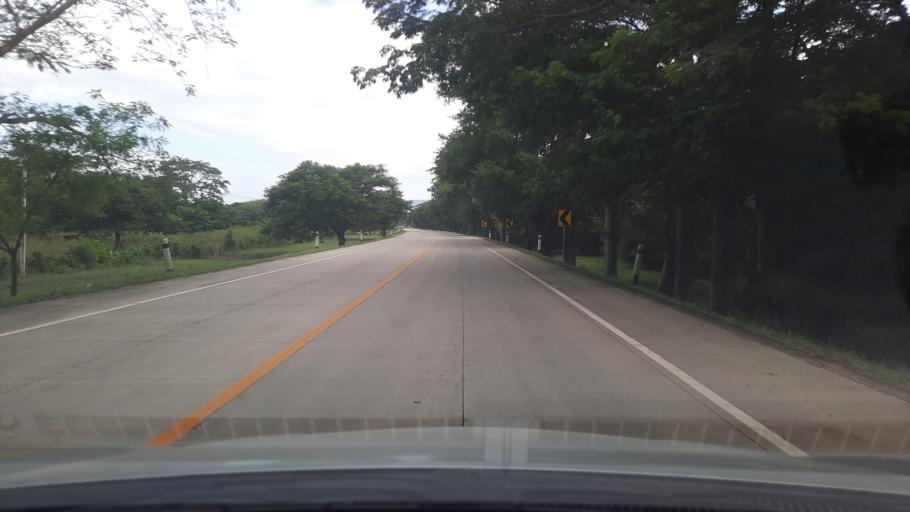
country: NI
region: Chinandega
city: Somotillo
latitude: 12.8282
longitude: -86.8971
